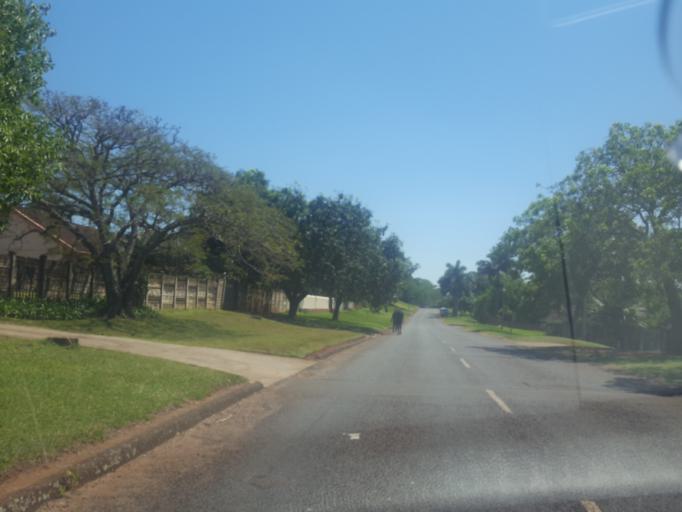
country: ZA
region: KwaZulu-Natal
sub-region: uThungulu District Municipality
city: Empangeni
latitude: -28.7578
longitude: 31.9054
